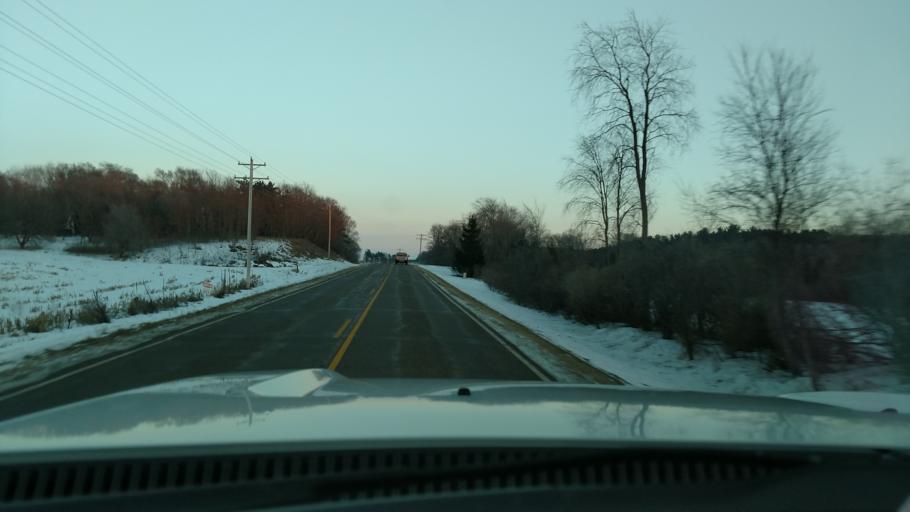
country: US
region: Wisconsin
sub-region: Saint Croix County
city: Roberts
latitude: 44.9134
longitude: -92.5255
